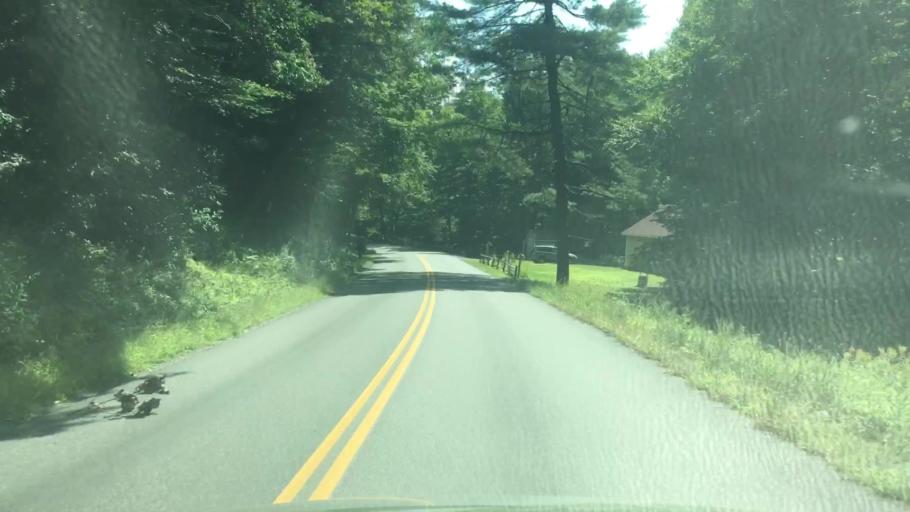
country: US
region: Vermont
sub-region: Windham County
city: West Brattleboro
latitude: 42.8062
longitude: -72.6089
